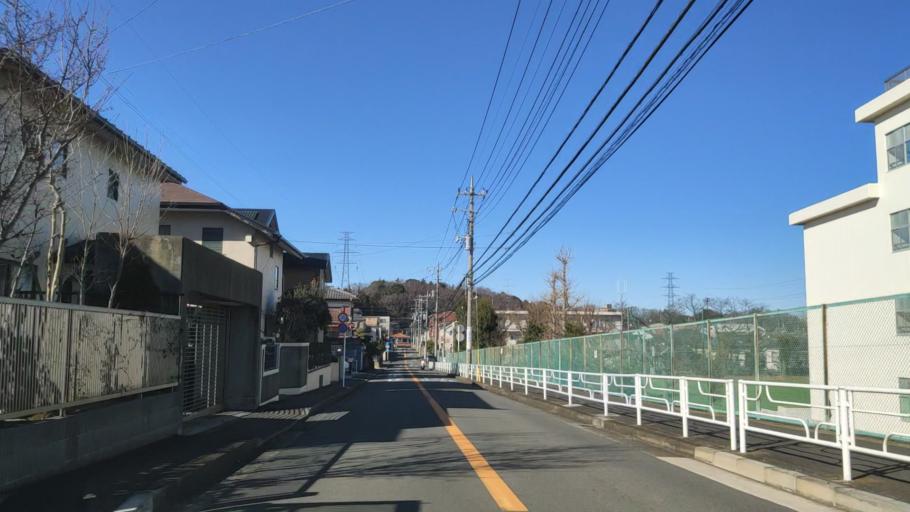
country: JP
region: Kanagawa
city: Minami-rinkan
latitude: 35.5102
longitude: 139.4987
